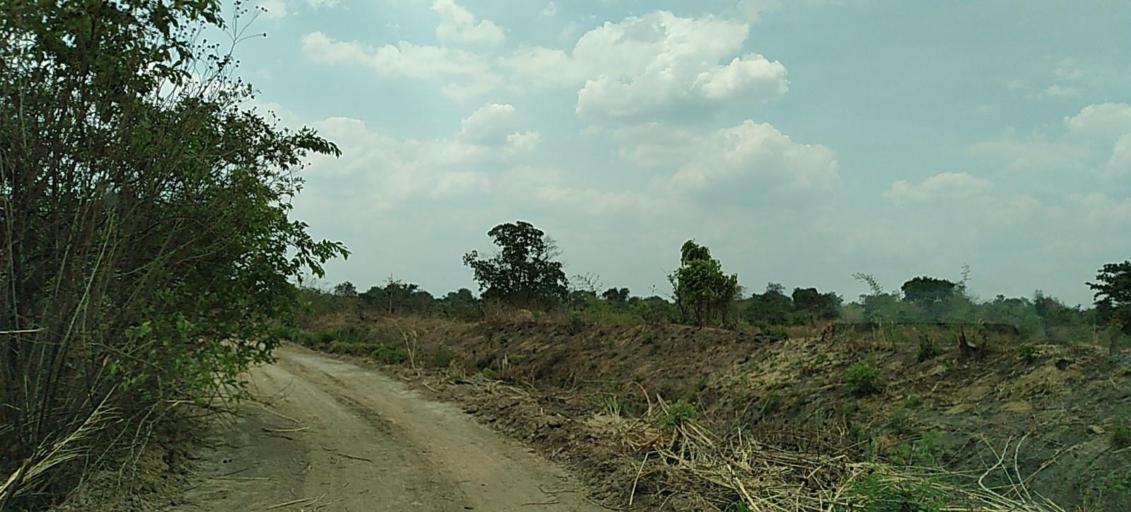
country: ZM
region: Copperbelt
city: Chililabombwe
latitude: -12.3531
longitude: 27.8029
